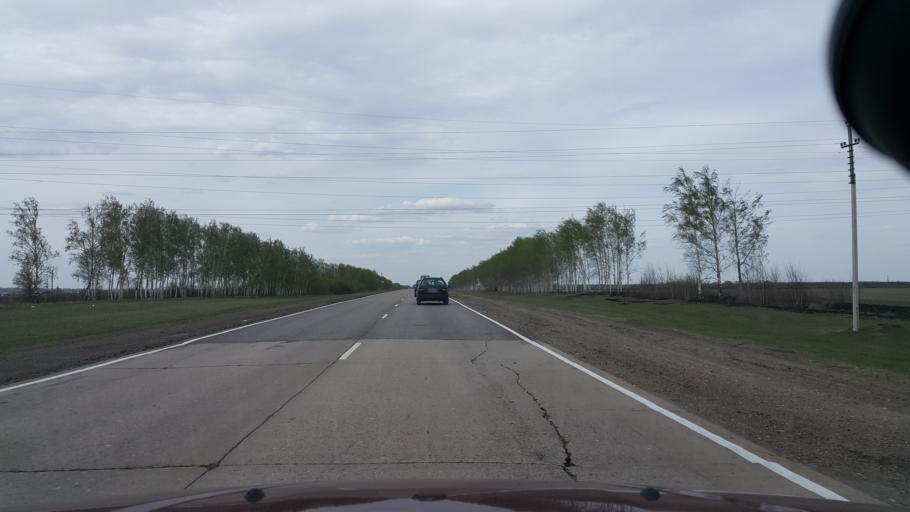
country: RU
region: Tambov
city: Pokrovo-Prigorodnoye
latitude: 52.6366
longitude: 41.3418
